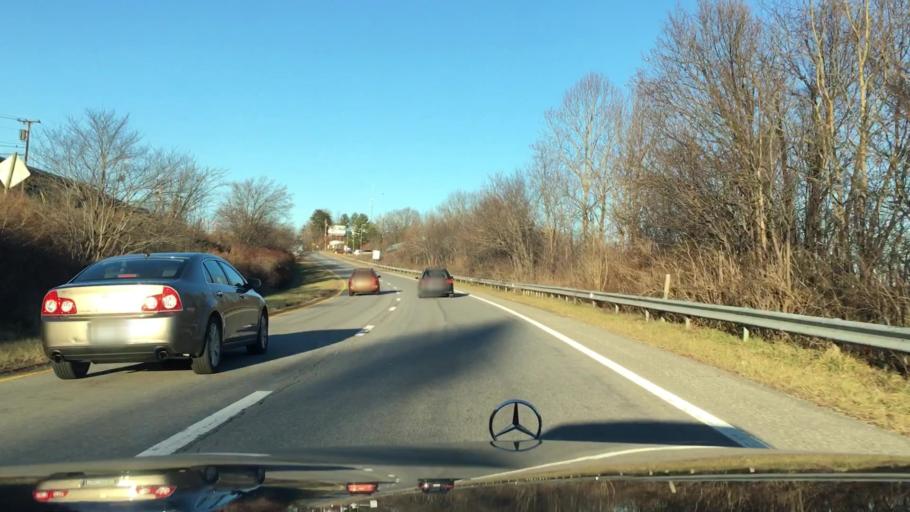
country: US
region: Virginia
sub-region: Montgomery County
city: Merrimac
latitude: 37.1813
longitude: -80.4114
